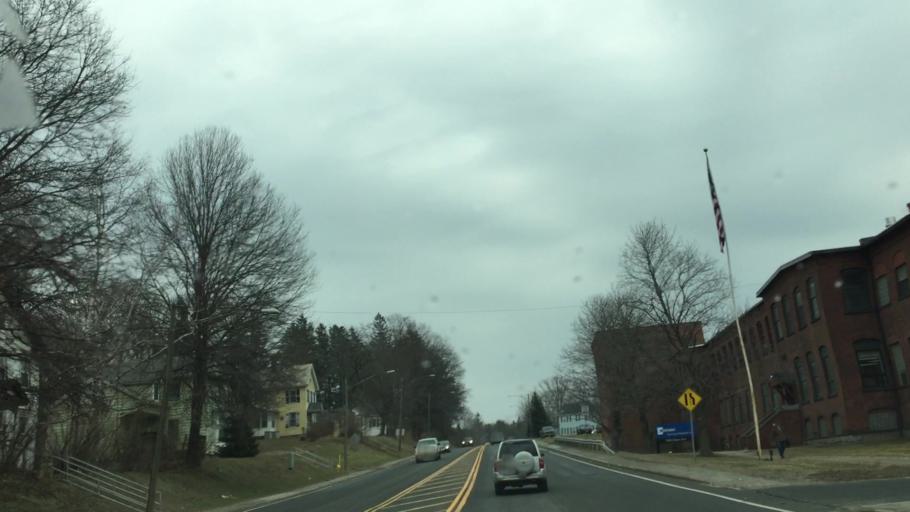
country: US
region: Massachusetts
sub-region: Berkshire County
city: Dalton
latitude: 42.4701
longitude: -73.1953
